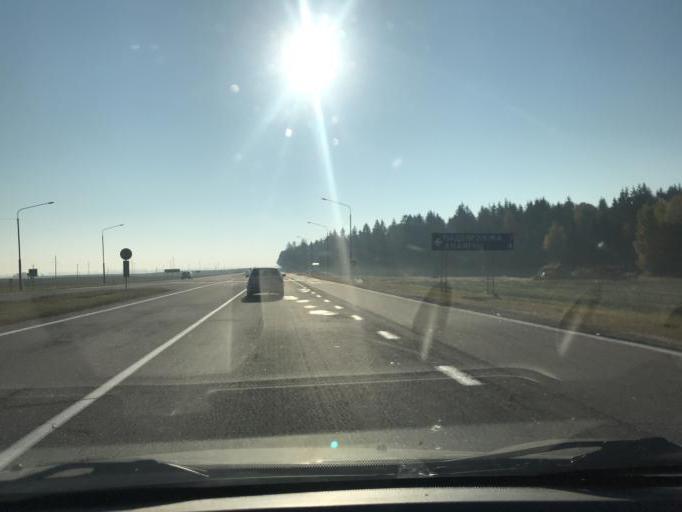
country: BY
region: Minsk
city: Mar''ina Horka
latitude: 53.6117
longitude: 28.0644
